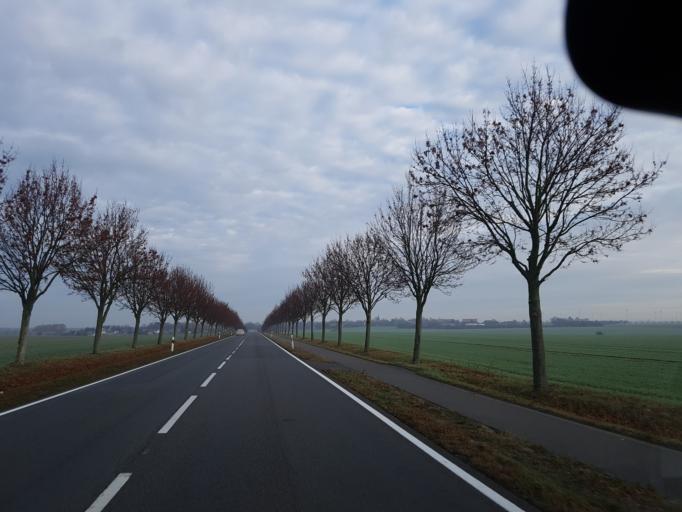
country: DE
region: Saxony-Anhalt
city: Kropstadt
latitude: 51.9922
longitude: 12.7693
